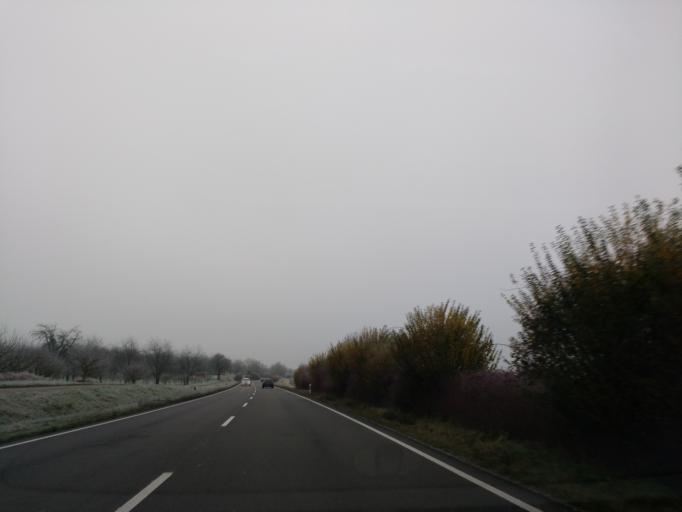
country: DE
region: Baden-Wuerttemberg
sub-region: Freiburg Region
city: Appenweier
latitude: 48.5380
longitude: 8.0153
